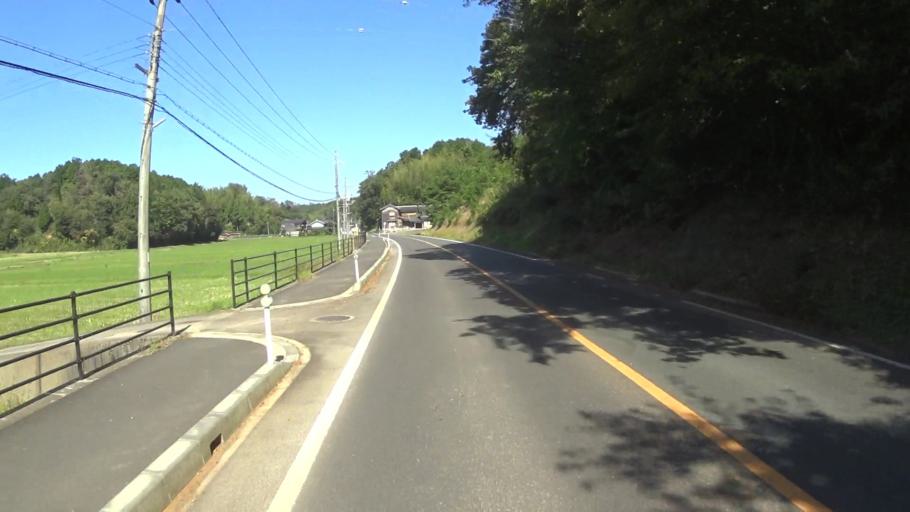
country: JP
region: Kyoto
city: Miyazu
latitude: 35.6503
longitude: 135.0684
